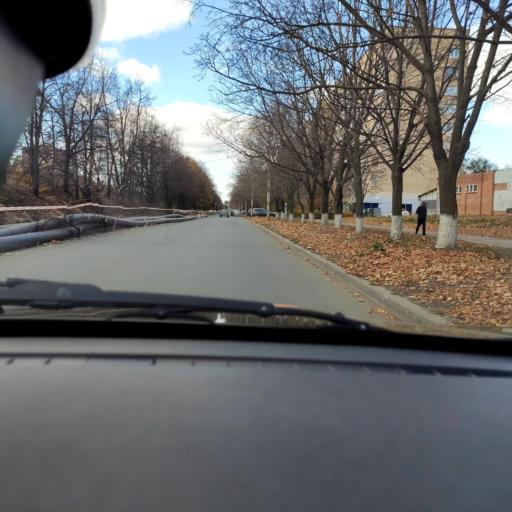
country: RU
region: Samara
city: Tol'yatti
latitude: 53.5213
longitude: 49.2684
